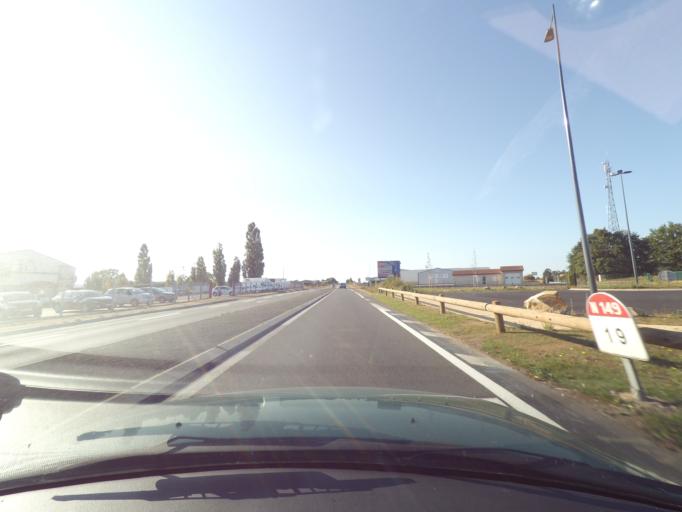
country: FR
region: Poitou-Charentes
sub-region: Departement des Deux-Sevres
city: Viennay
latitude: 46.6700
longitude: -0.2558
